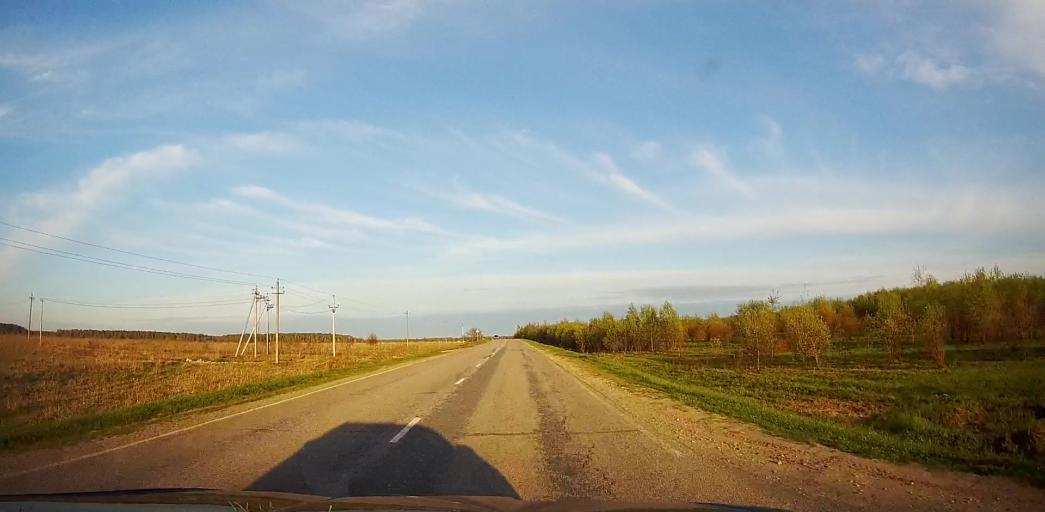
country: RU
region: Moskovskaya
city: Meshcherino
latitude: 55.2438
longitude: 38.3266
